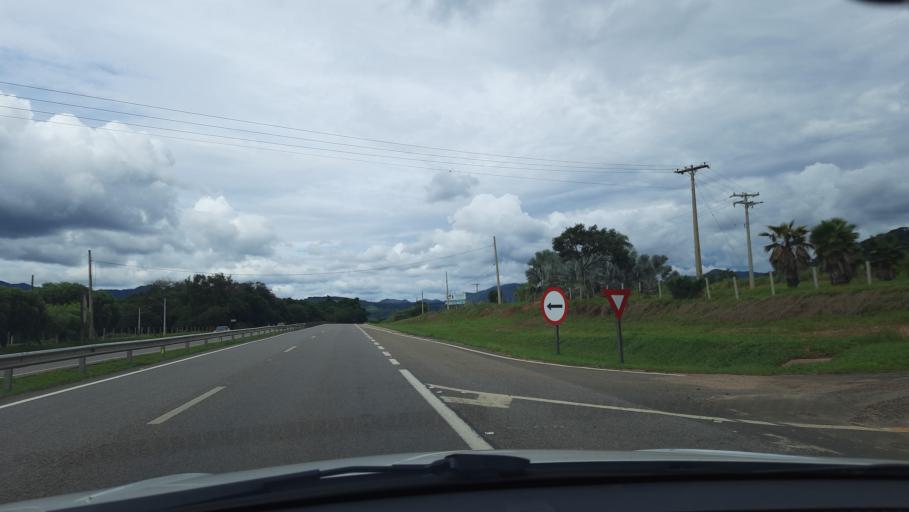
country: BR
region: Sao Paulo
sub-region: Sao Joao Da Boa Vista
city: Sao Joao da Boa Vista
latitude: -21.9640
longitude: -46.7378
